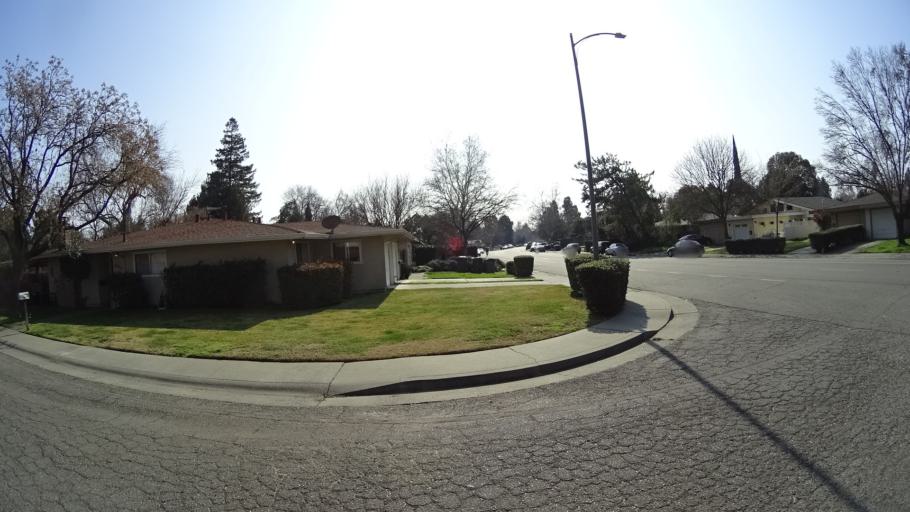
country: US
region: California
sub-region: Yolo County
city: Davis
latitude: 38.5526
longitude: -121.7705
